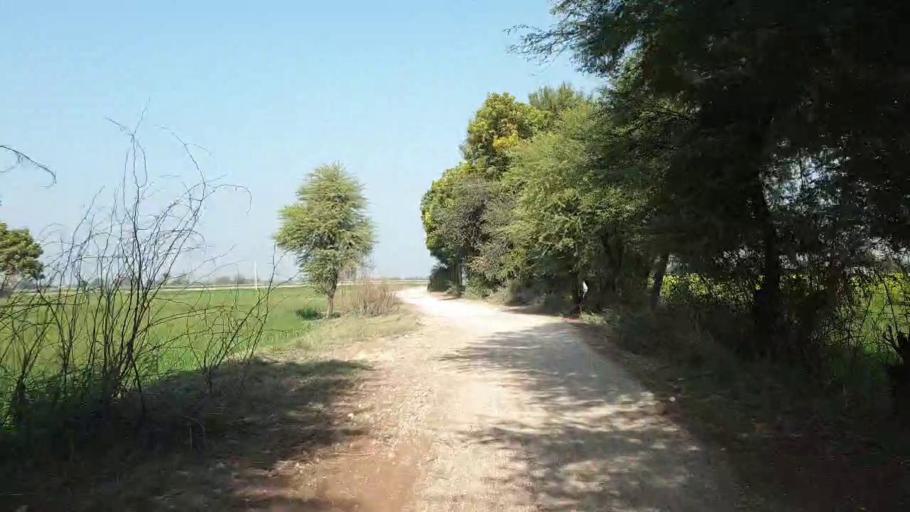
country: PK
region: Sindh
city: Hala
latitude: 25.9241
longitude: 68.4063
